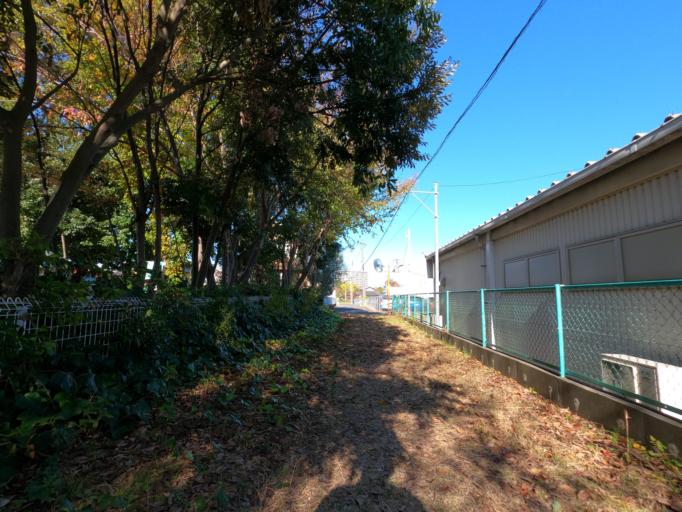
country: JP
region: Ibaraki
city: Moriya
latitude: 35.9456
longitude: 139.9915
